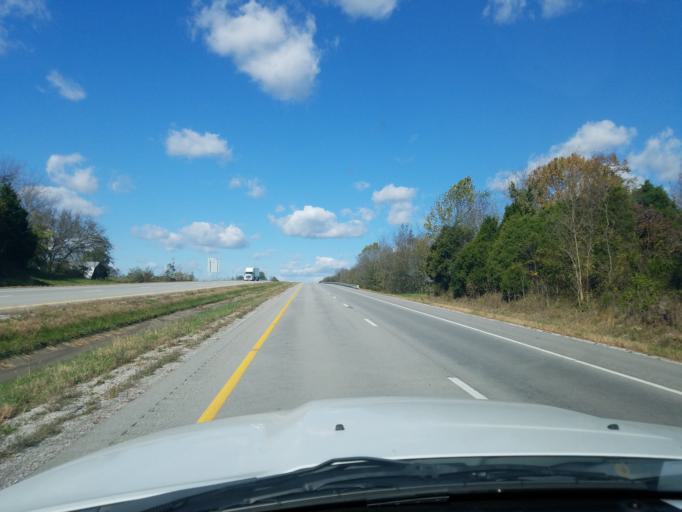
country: US
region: Kentucky
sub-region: Barren County
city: Glasgow
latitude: 36.9999
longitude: -85.9966
